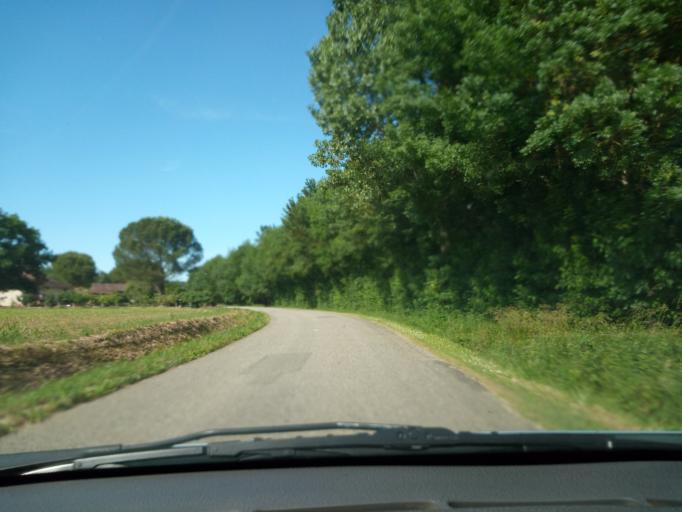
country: FR
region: Midi-Pyrenees
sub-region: Departement du Tarn-et-Garonne
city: Molieres
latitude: 44.2047
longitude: 1.3061
